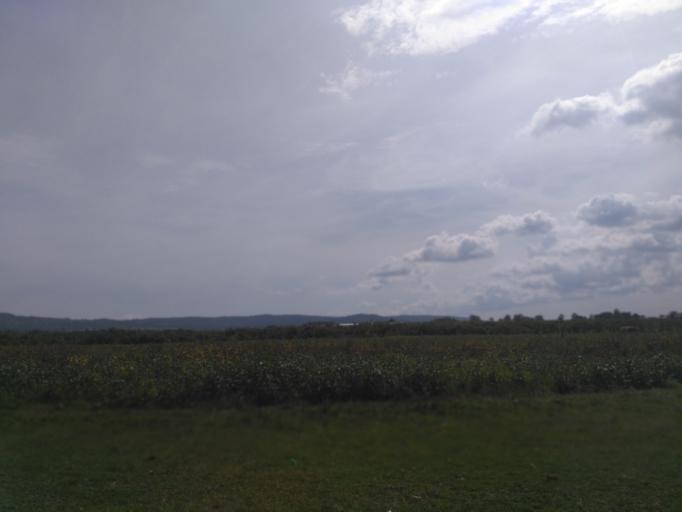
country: UG
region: Eastern Region
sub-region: Jinja District
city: Jinja
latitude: 0.4229
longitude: 33.2230
